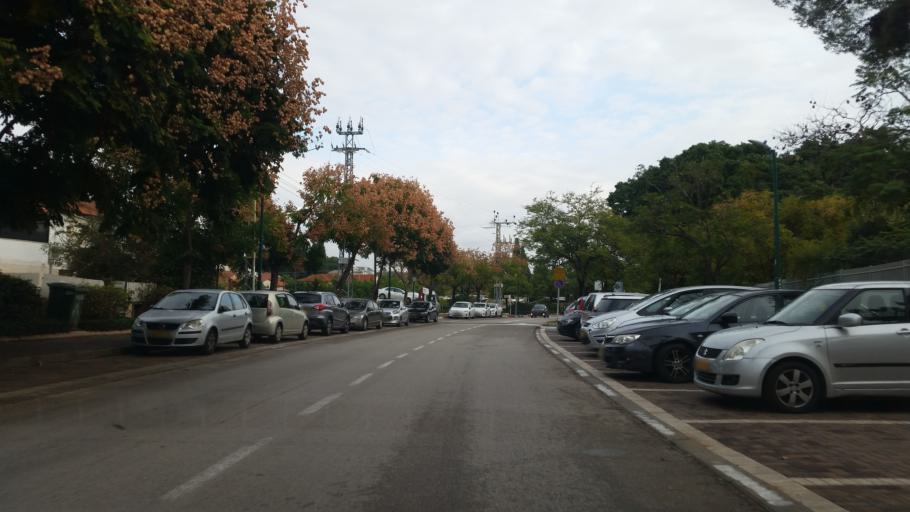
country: IL
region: Tel Aviv
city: Ramat HaSharon
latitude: 32.1638
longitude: 34.8550
